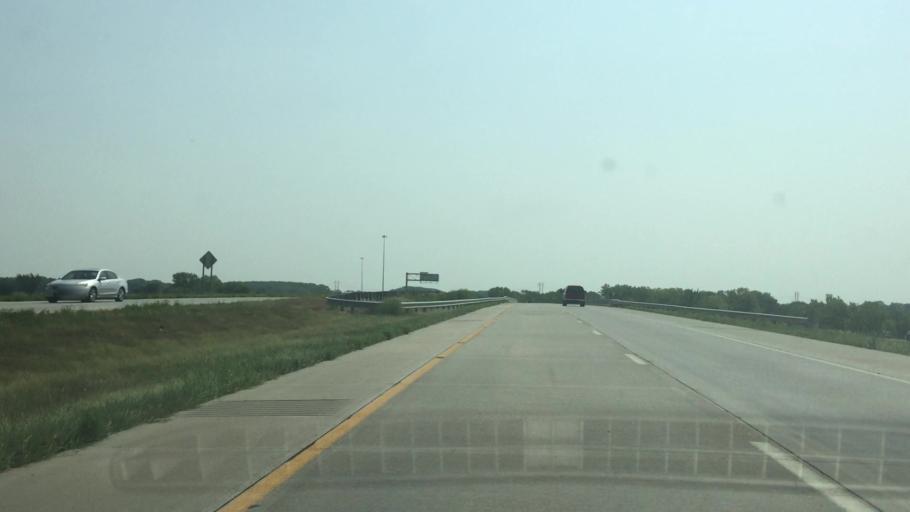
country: US
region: Kansas
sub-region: Lyon County
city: Emporia
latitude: 38.4112
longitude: -96.1408
